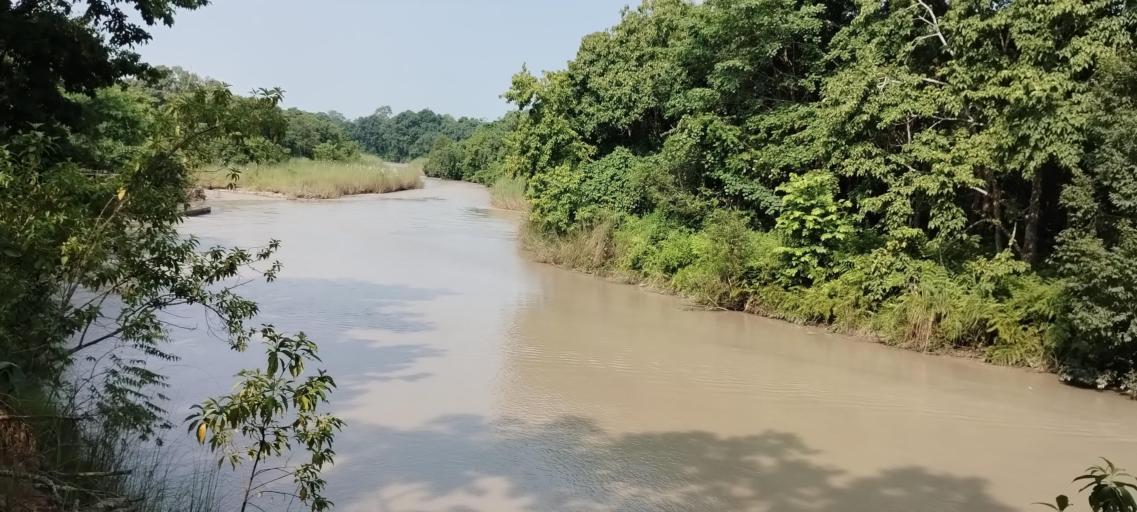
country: NP
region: Far Western
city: Tikapur
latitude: 28.4731
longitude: 81.2516
